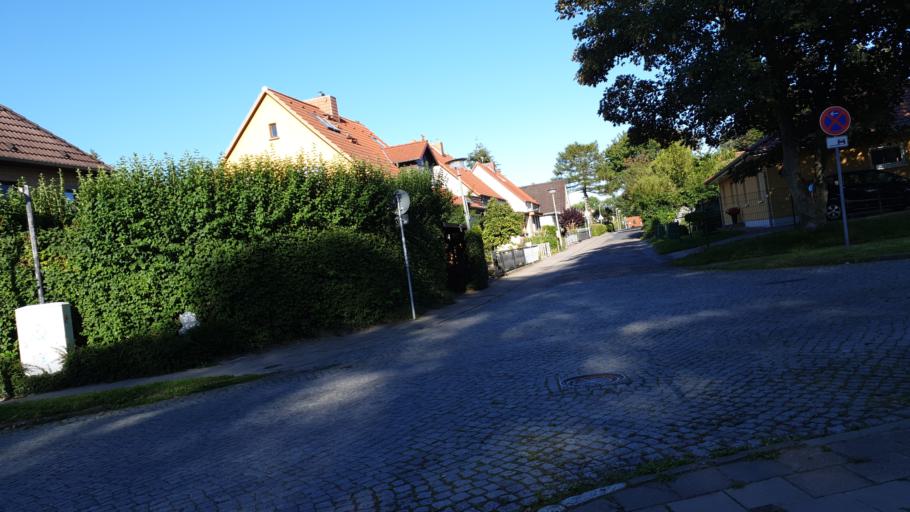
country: DE
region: Mecklenburg-Vorpommern
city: Stralsund
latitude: 54.3276
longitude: 13.0760
